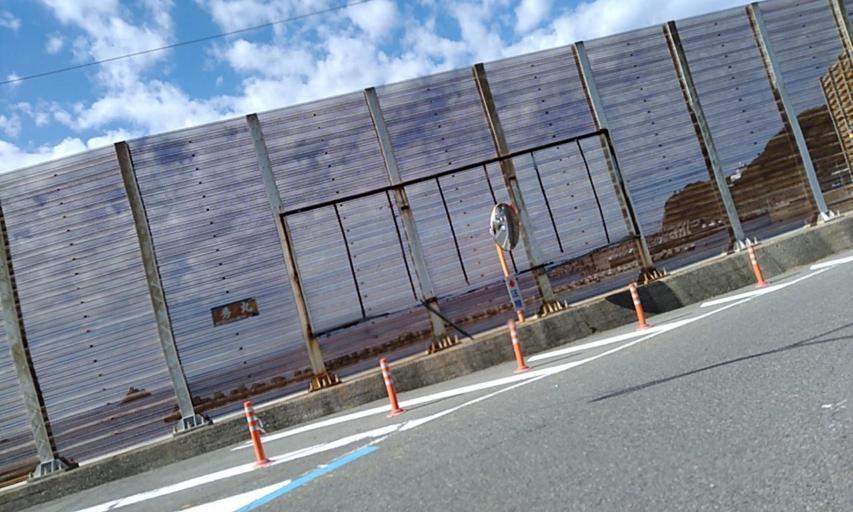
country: JP
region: Wakayama
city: Gobo
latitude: 33.9677
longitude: 135.0865
